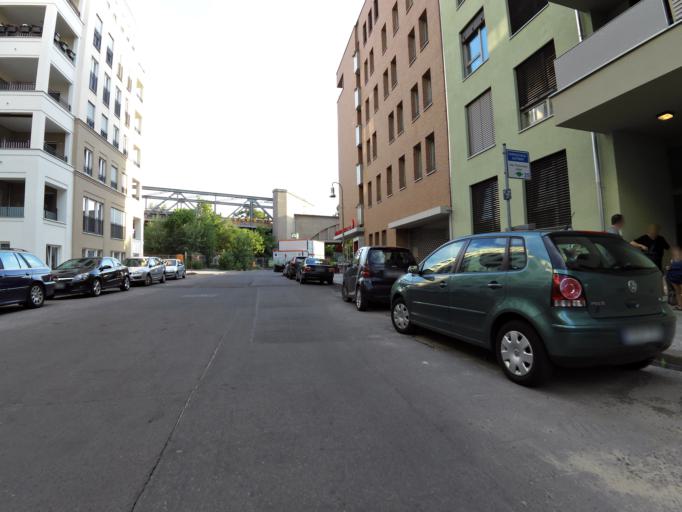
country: DE
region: Berlin
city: Tiergarten Bezirk
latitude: 52.5004
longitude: 13.3709
